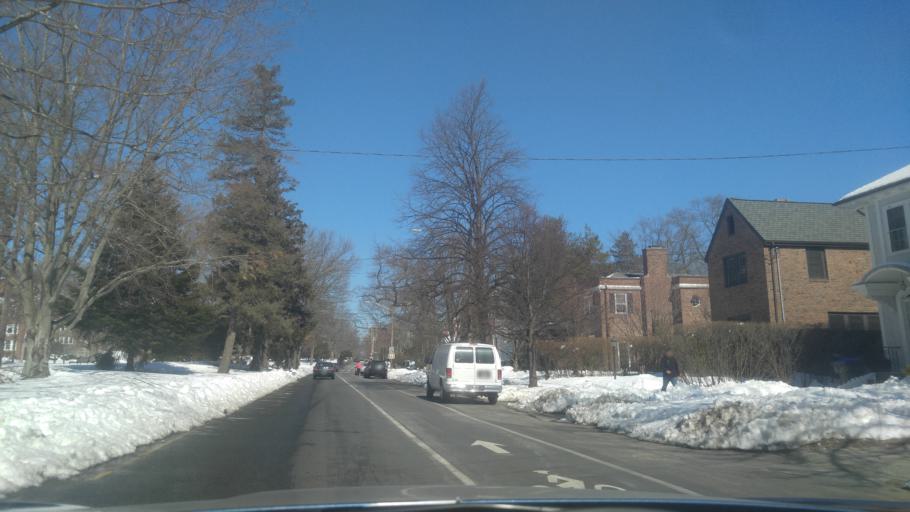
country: US
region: Rhode Island
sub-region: Providence County
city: East Providence
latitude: 41.8354
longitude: -71.3842
